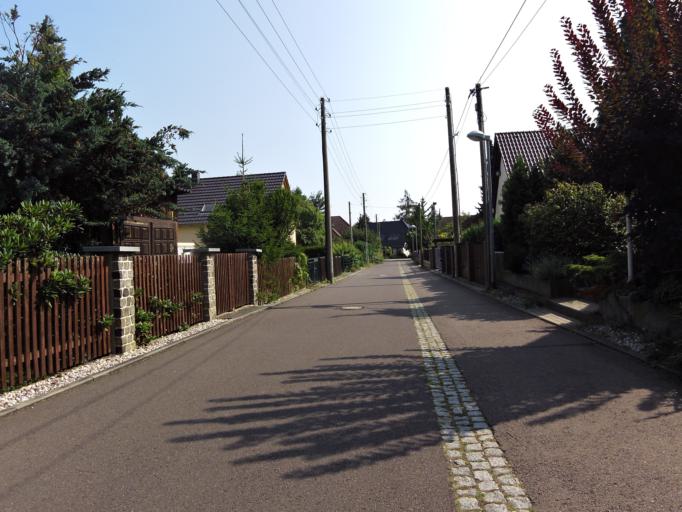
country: DE
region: Saxony
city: Rackwitz
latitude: 51.3899
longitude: 12.3838
